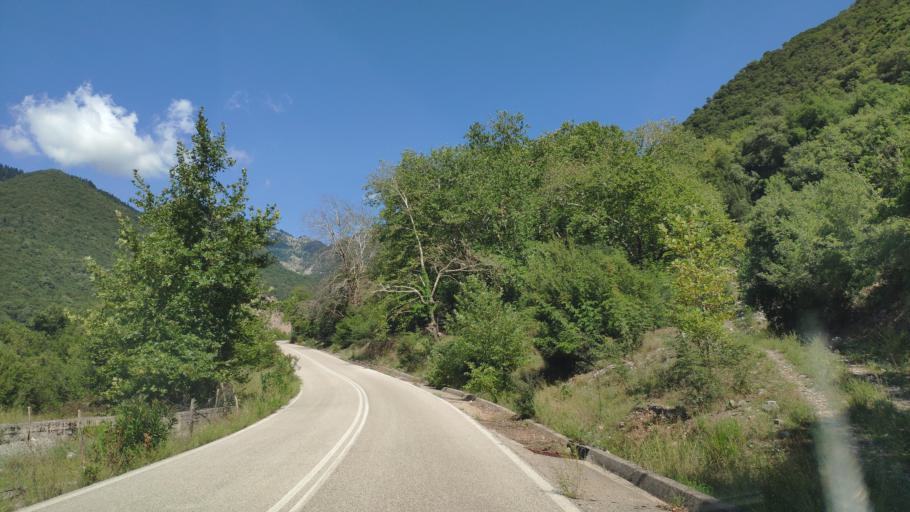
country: GR
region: Central Greece
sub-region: Nomos Evrytanias
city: Kerasochori
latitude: 39.0295
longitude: 21.6015
